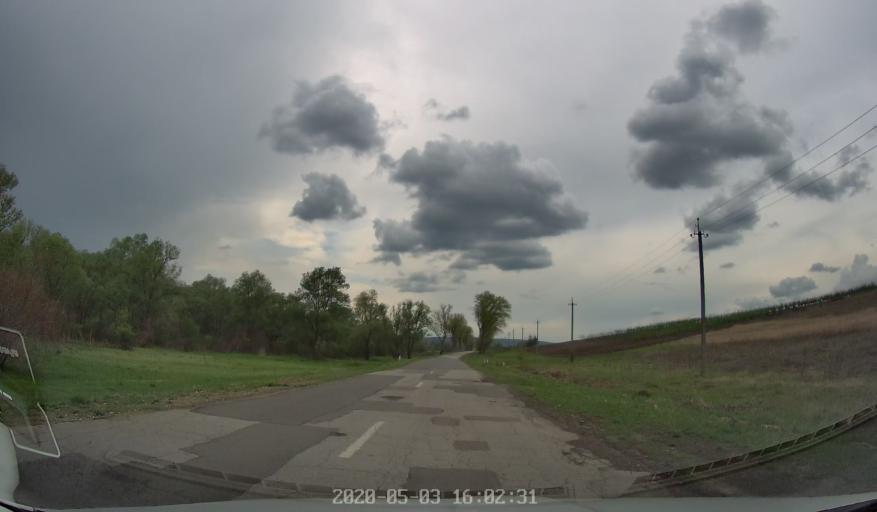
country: MD
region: Stinga Nistrului
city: Bucovat
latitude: 47.1735
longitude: 28.3945
